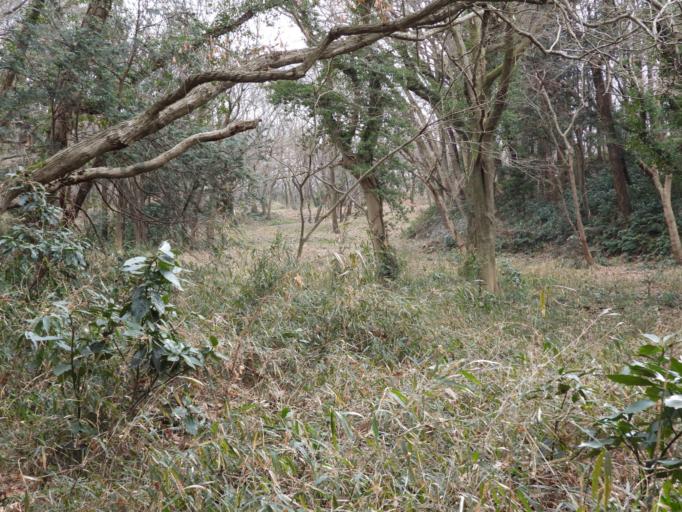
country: JP
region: Ibaraki
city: Naka
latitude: 36.0792
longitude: 140.1647
